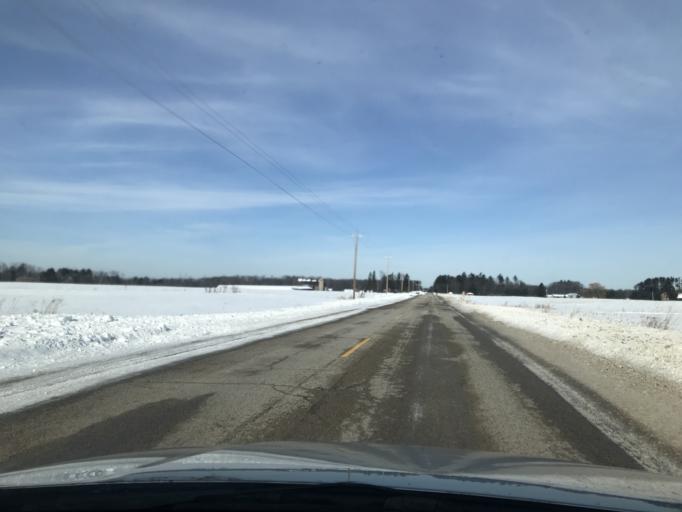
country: US
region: Wisconsin
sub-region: Oconto County
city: Oconto Falls
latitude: 45.1286
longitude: -88.1777
